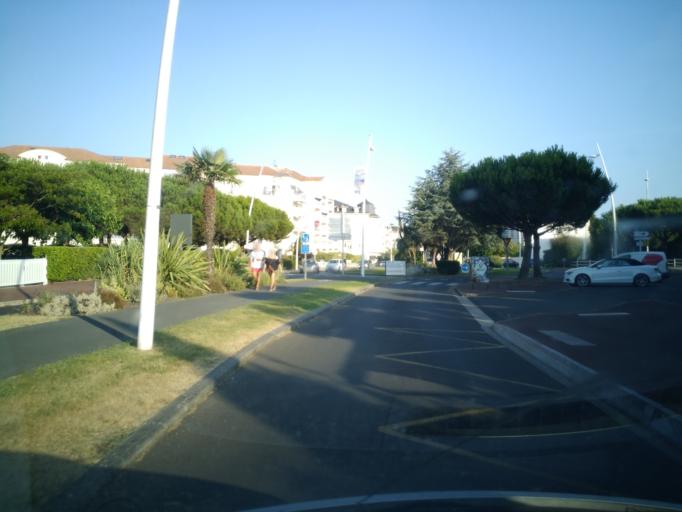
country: FR
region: Poitou-Charentes
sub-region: Departement de la Charente-Maritime
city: Vaux-sur-Mer
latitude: 45.6293
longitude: -1.0543
